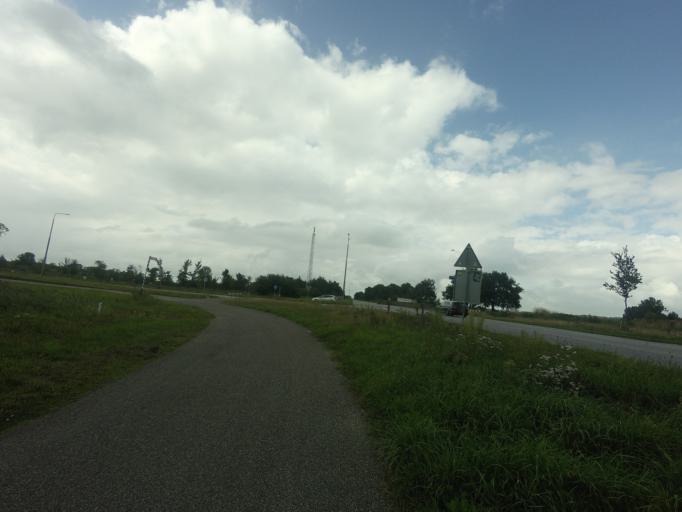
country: NL
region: Friesland
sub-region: Gemeente Skarsterlan
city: Joure
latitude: 52.9647
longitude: 5.7752
